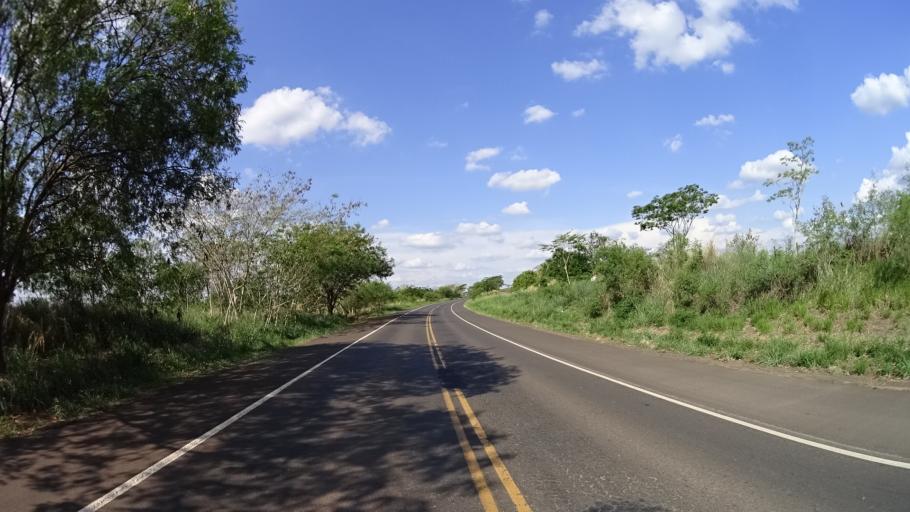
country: BR
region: Sao Paulo
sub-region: Urupes
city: Urupes
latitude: -21.0097
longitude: -49.2245
